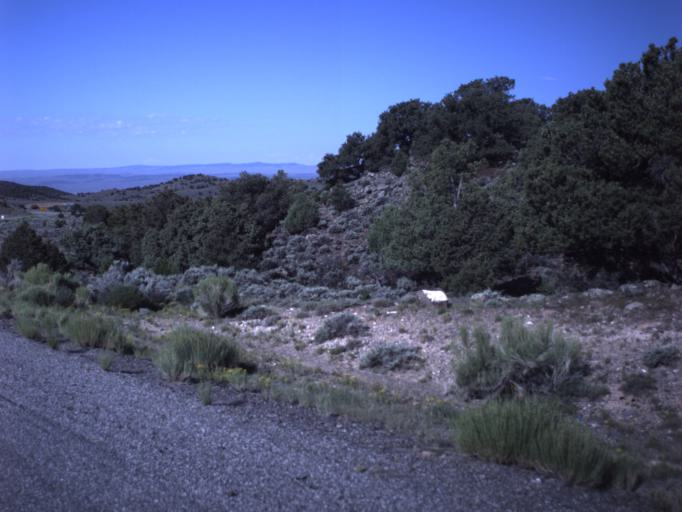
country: US
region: Utah
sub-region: Wayne County
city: Loa
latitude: 38.4943
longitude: -111.5356
